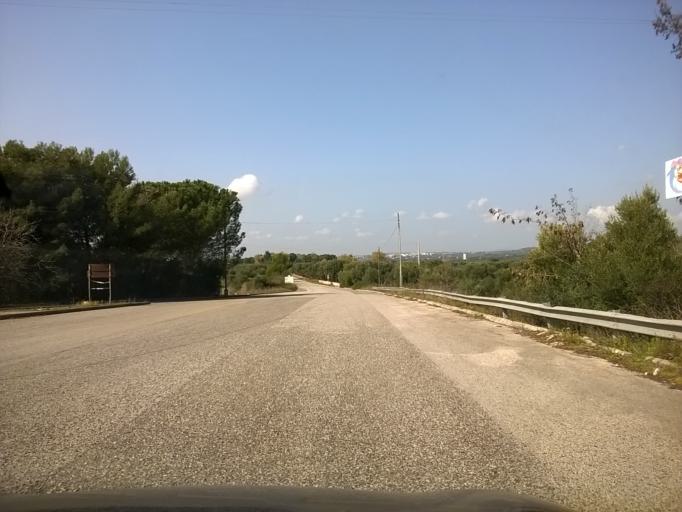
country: IT
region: Apulia
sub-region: Provincia di Taranto
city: Paolo VI
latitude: 40.5459
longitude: 17.2730
